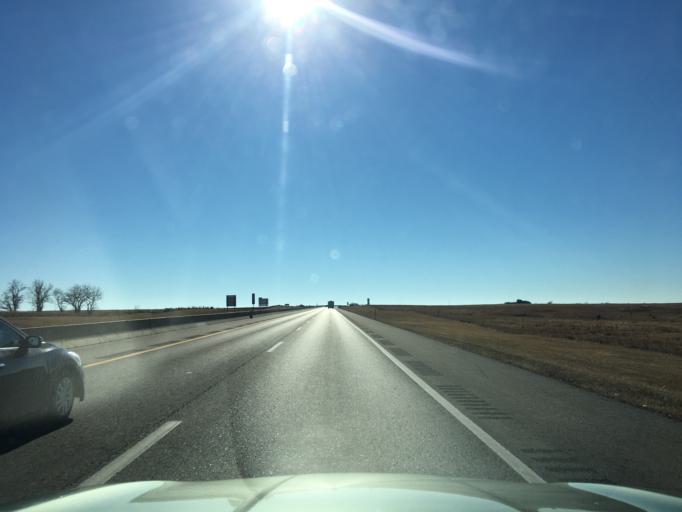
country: US
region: Kansas
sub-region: Sumner County
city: Wellington
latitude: 37.0516
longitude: -97.3384
